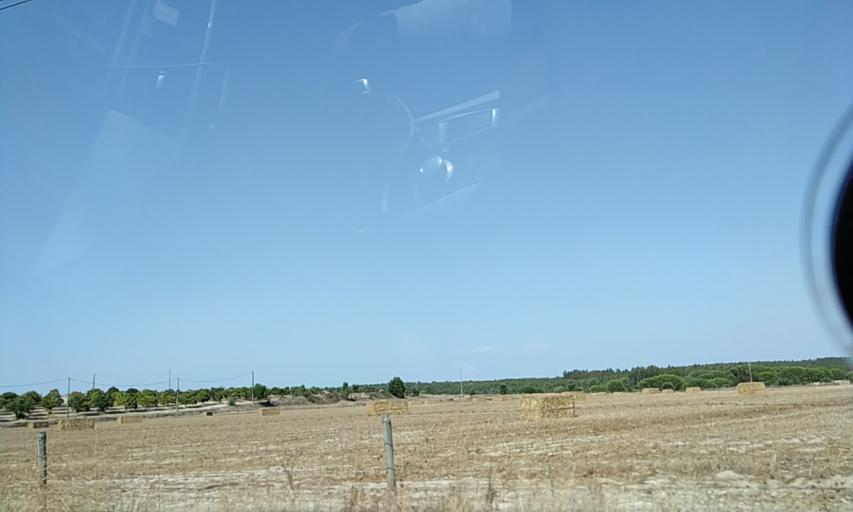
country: PT
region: Evora
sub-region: Vendas Novas
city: Vendas Novas
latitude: 38.7193
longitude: -8.6188
